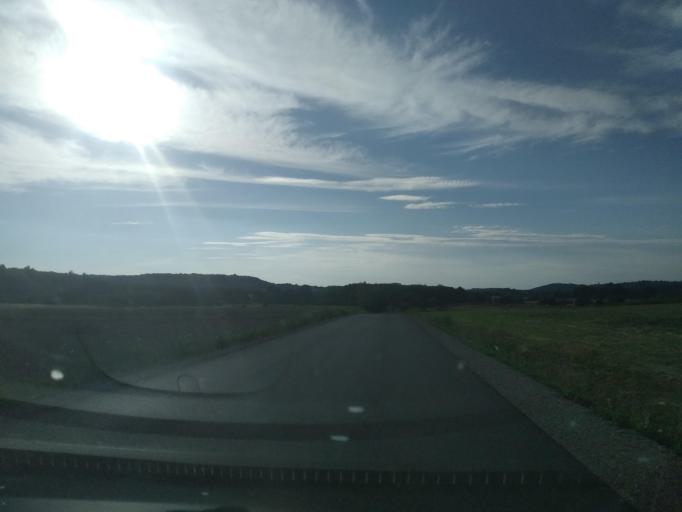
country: PL
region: Subcarpathian Voivodeship
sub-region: Powiat sanocki
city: Strachocina
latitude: 49.5918
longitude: 22.1042
